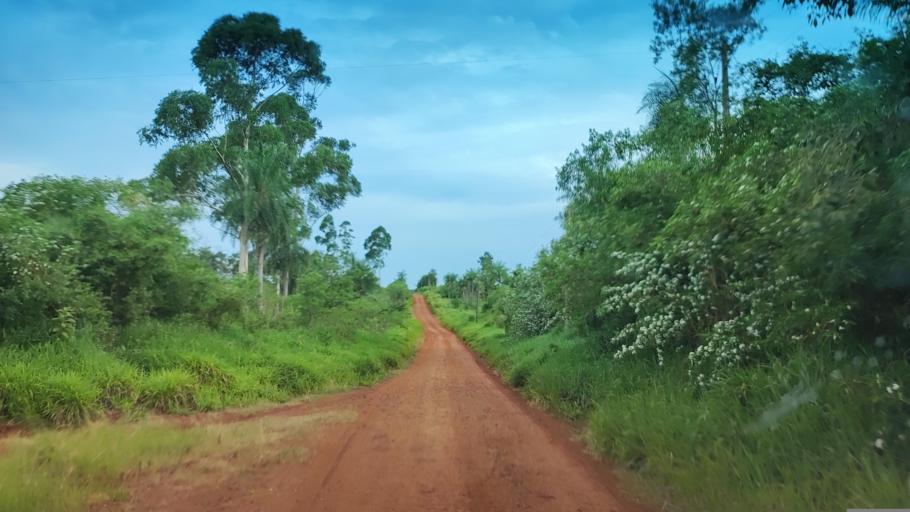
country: AR
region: Misiones
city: Gobernador Roca
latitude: -27.1653
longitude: -55.4559
